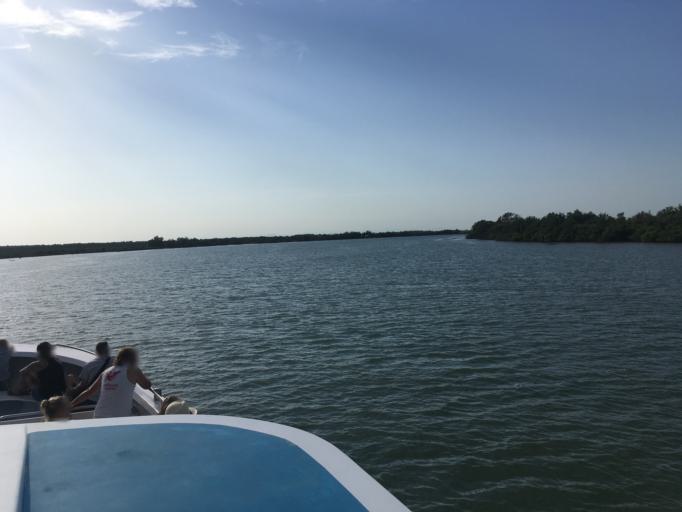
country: FR
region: Provence-Alpes-Cote d'Azur
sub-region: Departement des Bouches-du-Rhone
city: Saintes-Maries-de-la-Mer
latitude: 43.4667
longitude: 4.3835
